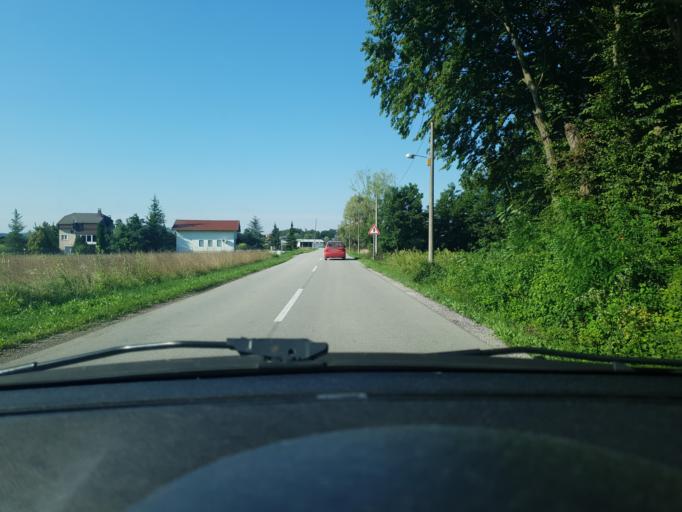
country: HR
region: Zagrebacka
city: Jakovlje
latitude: 45.9581
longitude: 15.8540
